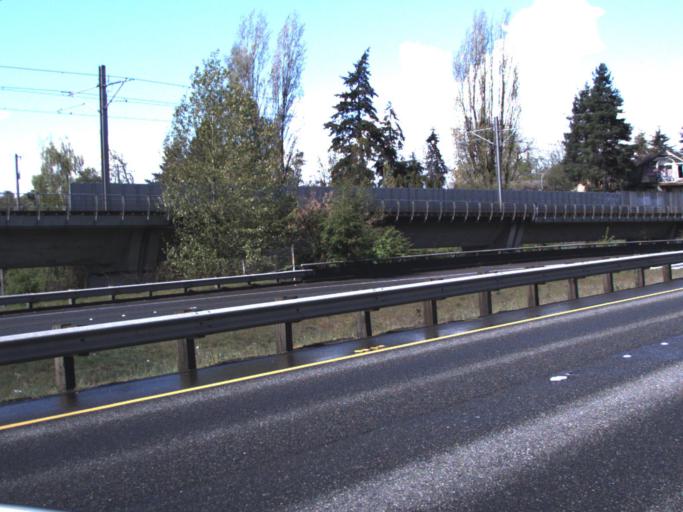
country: US
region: Washington
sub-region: King County
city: Tukwila
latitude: 47.4848
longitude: -122.2739
